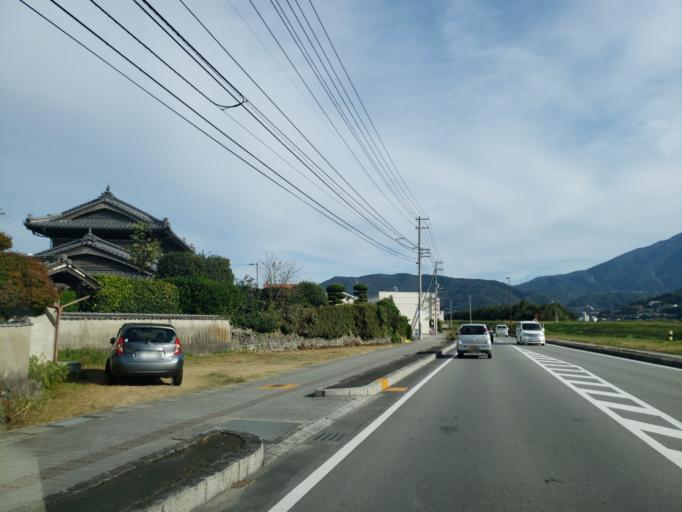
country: JP
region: Tokushima
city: Wakimachi
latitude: 34.0656
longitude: 134.1499
